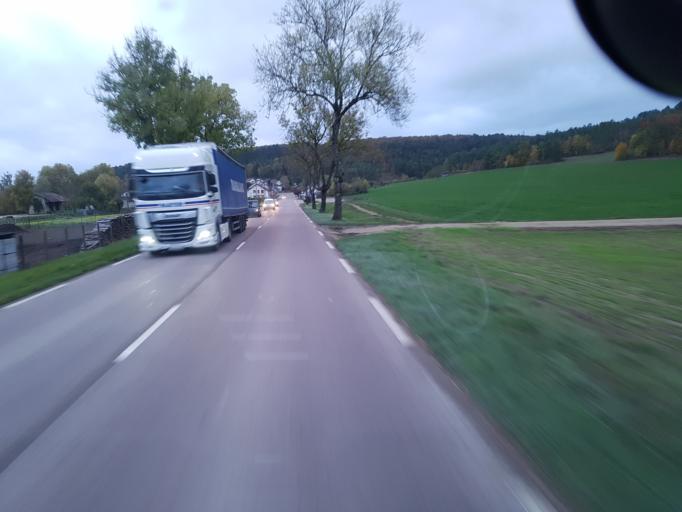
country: FR
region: Champagne-Ardenne
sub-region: Departement de l'Aube
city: Mussy-sur-Seine
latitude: 47.9917
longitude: 4.4837
